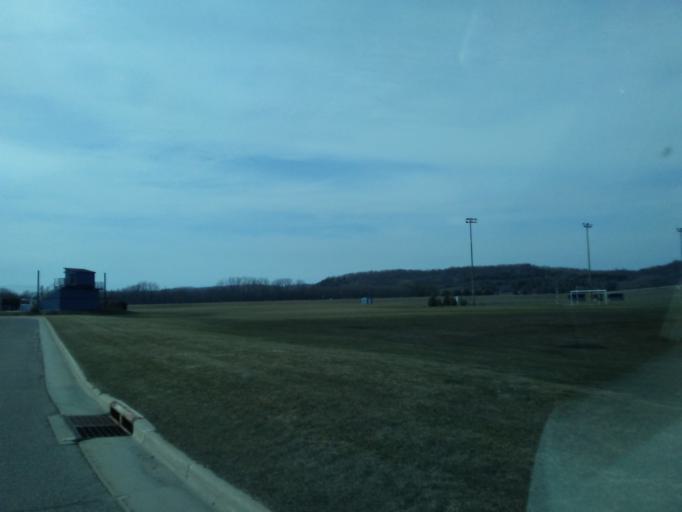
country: US
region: Iowa
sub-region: Winneshiek County
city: Decorah
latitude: 43.3158
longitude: -91.8065
